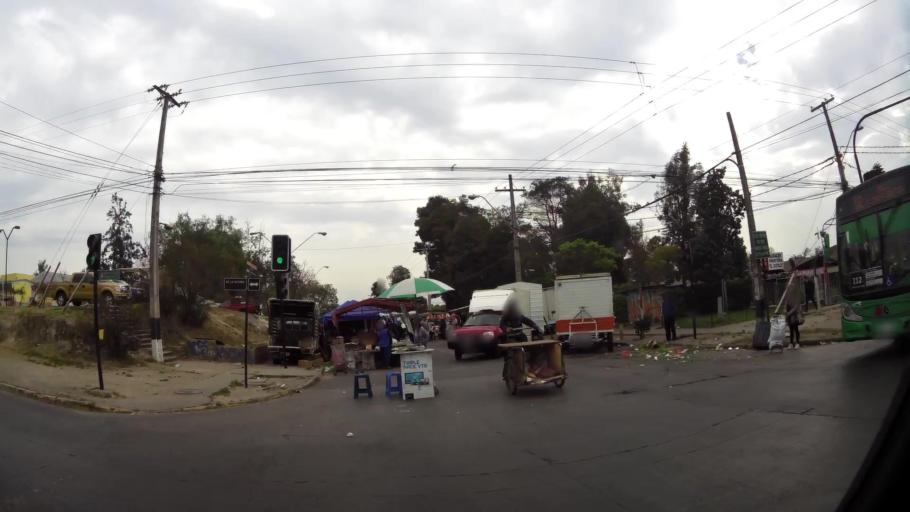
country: CL
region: Santiago Metropolitan
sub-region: Provincia de Santiago
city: Lo Prado
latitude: -33.5022
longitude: -70.7688
